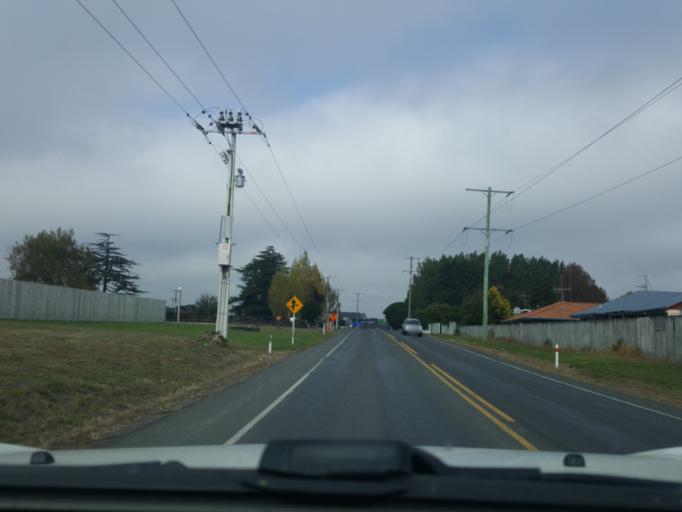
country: NZ
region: Waikato
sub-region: Hamilton City
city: Hamilton
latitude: -37.7468
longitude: 175.2925
